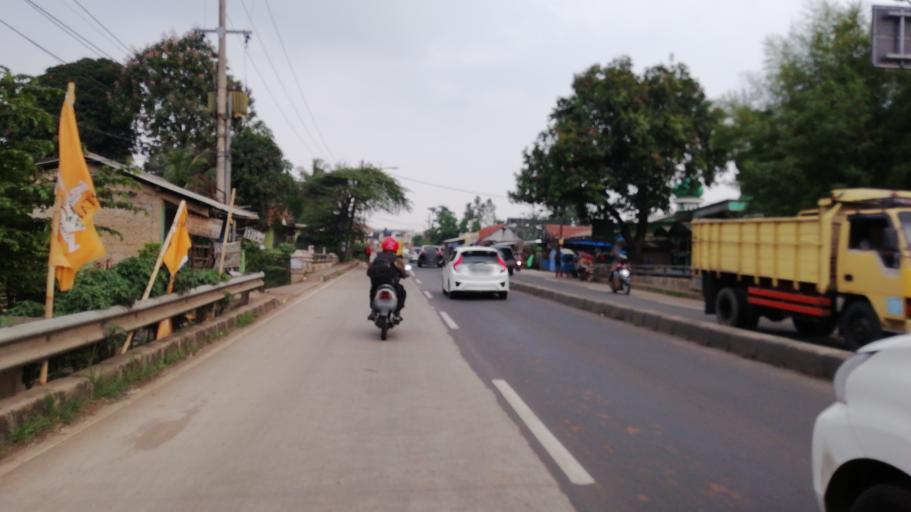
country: ID
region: West Java
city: Parung
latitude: -6.4942
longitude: 106.7487
